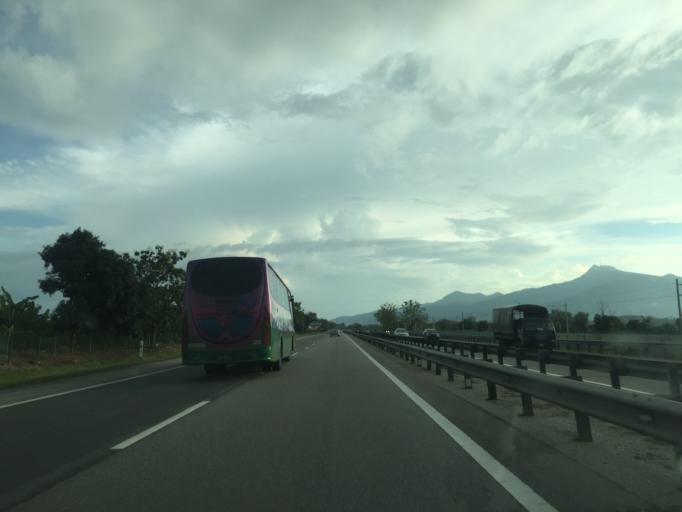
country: MY
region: Kedah
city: Gurun
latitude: 5.8851
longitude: 100.4774
